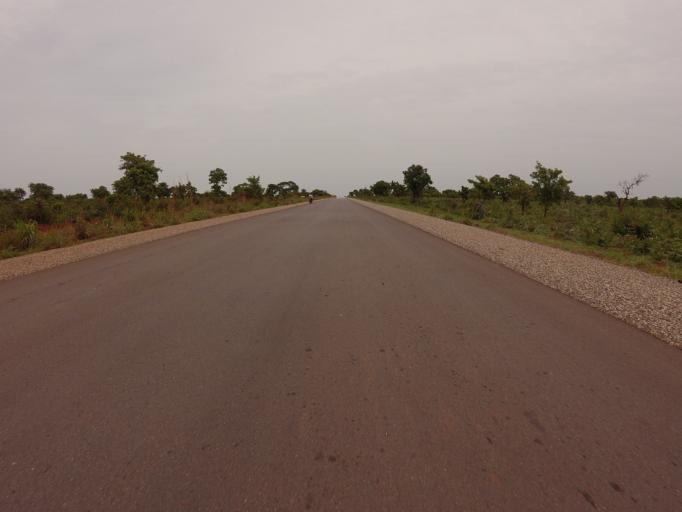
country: GH
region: Northern
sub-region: Yendi
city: Yendi
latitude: 8.9560
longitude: -0.0174
